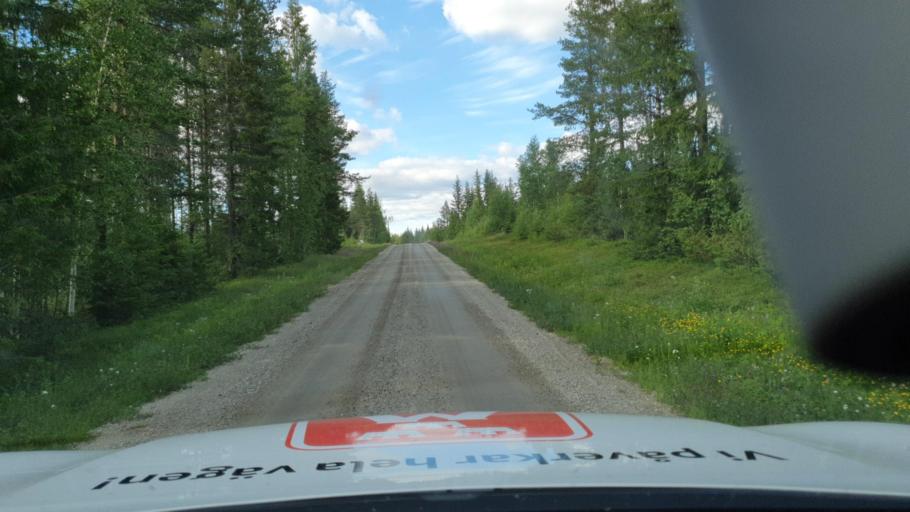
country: SE
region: Vaesterbotten
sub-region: Lycksele Kommun
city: Lycksele
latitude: 64.4746
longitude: 18.2849
